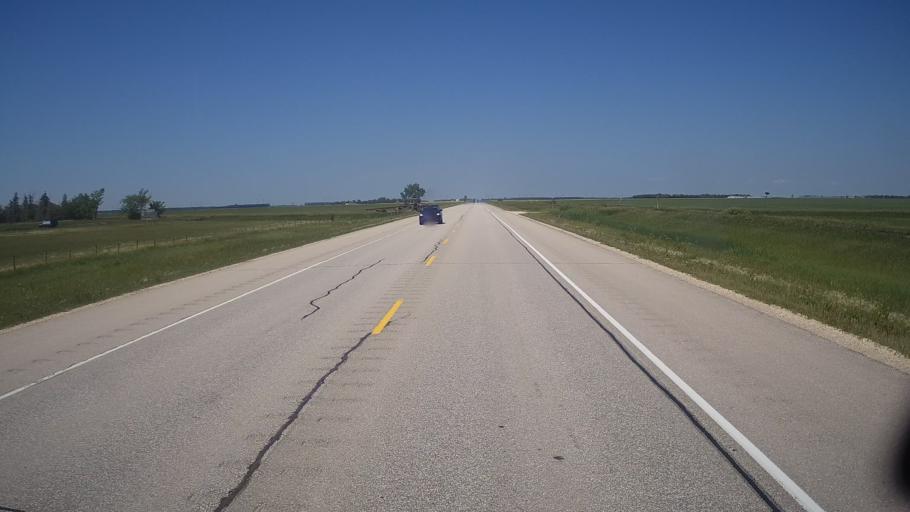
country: CA
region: Manitoba
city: Stonewall
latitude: 50.0188
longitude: -97.3729
